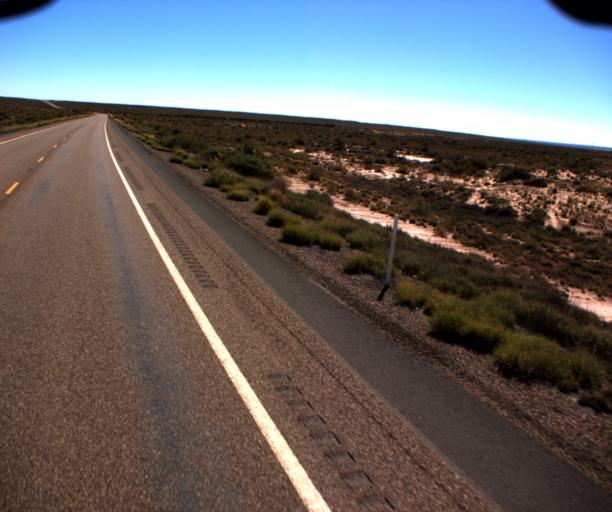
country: US
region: Arizona
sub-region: Navajo County
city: Holbrook
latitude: 35.0589
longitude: -110.0964
